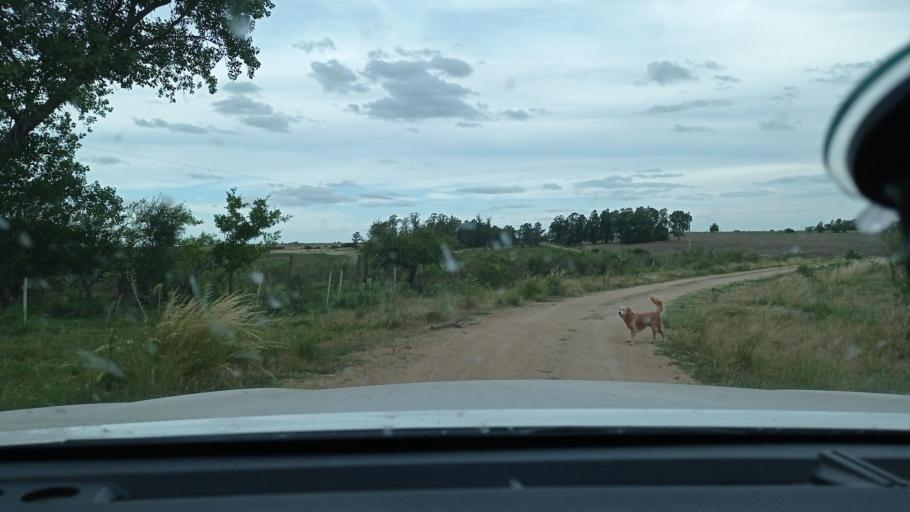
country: UY
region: Florida
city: Casupa
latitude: -34.1411
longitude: -55.7993
